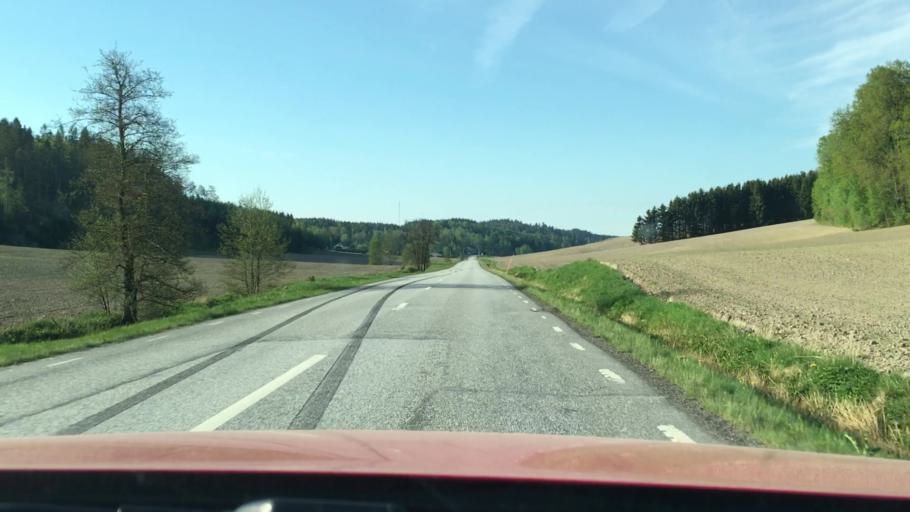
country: SE
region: Vaestra Goetaland
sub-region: Munkedals Kommun
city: Munkedal
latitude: 58.6128
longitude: 11.5587
